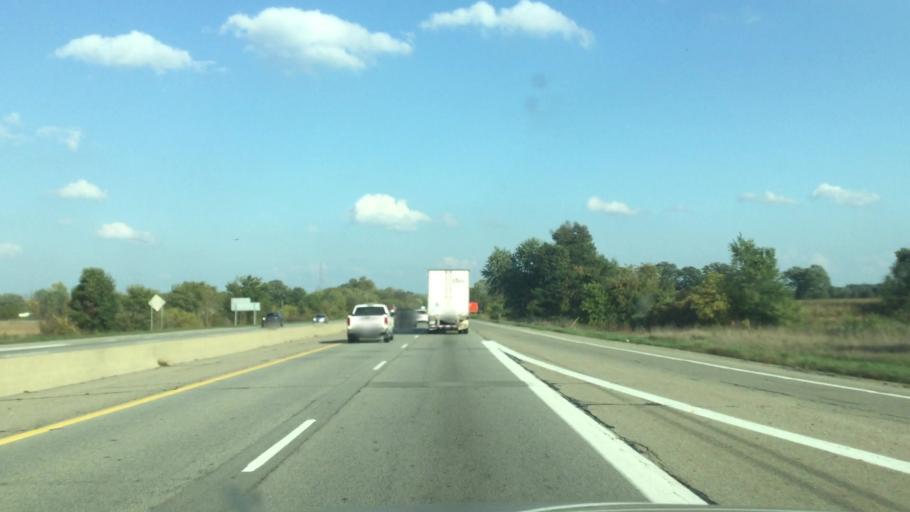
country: US
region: Michigan
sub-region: Jackson County
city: Spring Arbor
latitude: 42.2691
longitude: -84.5971
